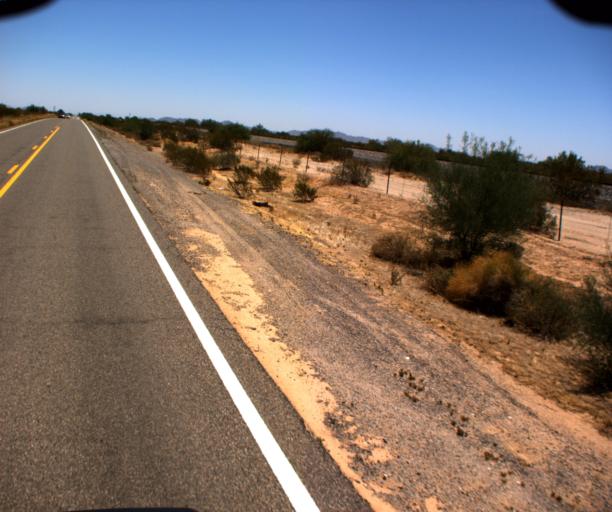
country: US
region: Arizona
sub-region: Pinal County
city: Maricopa
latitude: 33.0415
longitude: -112.3265
